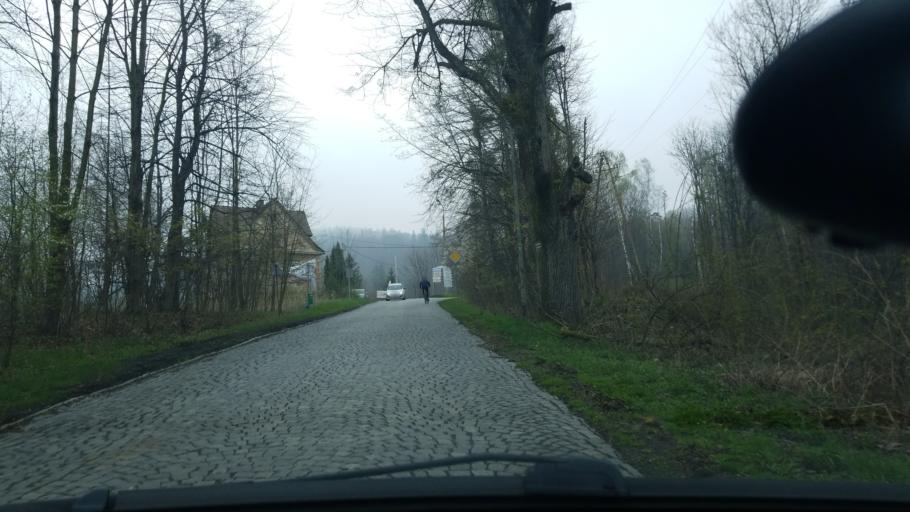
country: PL
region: Silesian Voivodeship
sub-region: Powiat cieszynski
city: Ustron
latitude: 49.7041
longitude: 18.8369
